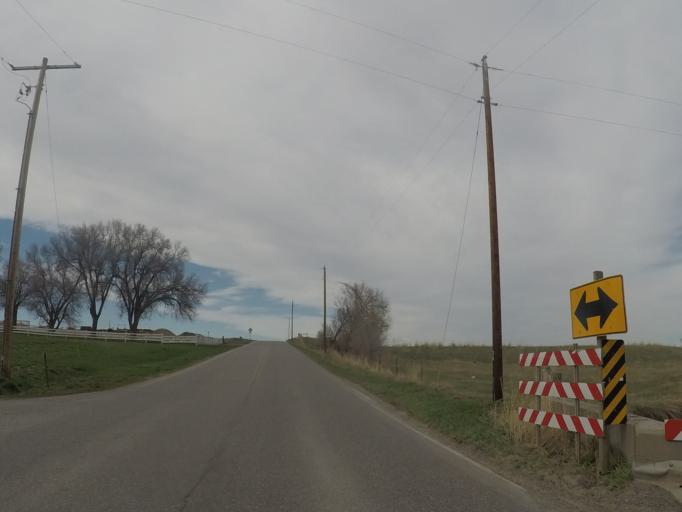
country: US
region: Montana
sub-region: Yellowstone County
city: Laurel
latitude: 45.7116
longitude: -108.6587
